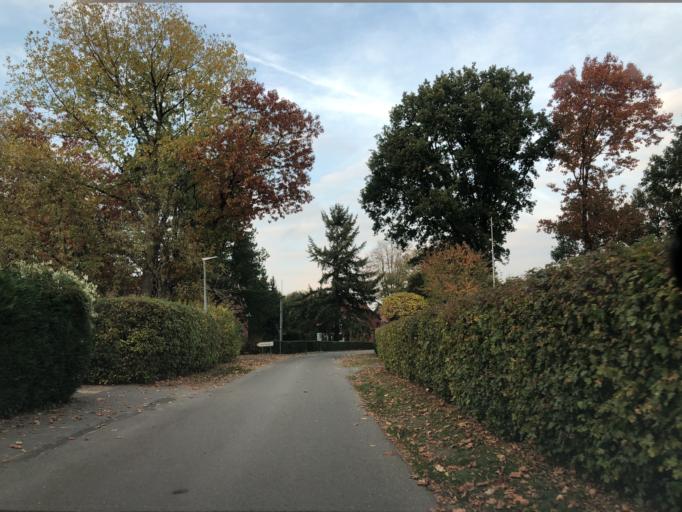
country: DE
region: Lower Saxony
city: Papenburg
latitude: 53.0413
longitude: 7.3924
